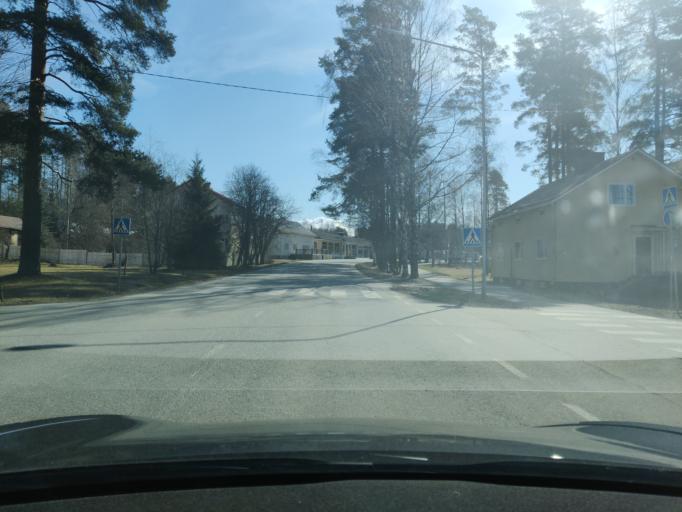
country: FI
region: Northern Savo
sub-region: Kuopio
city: Vehmersalmi
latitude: 62.7623
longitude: 28.0254
